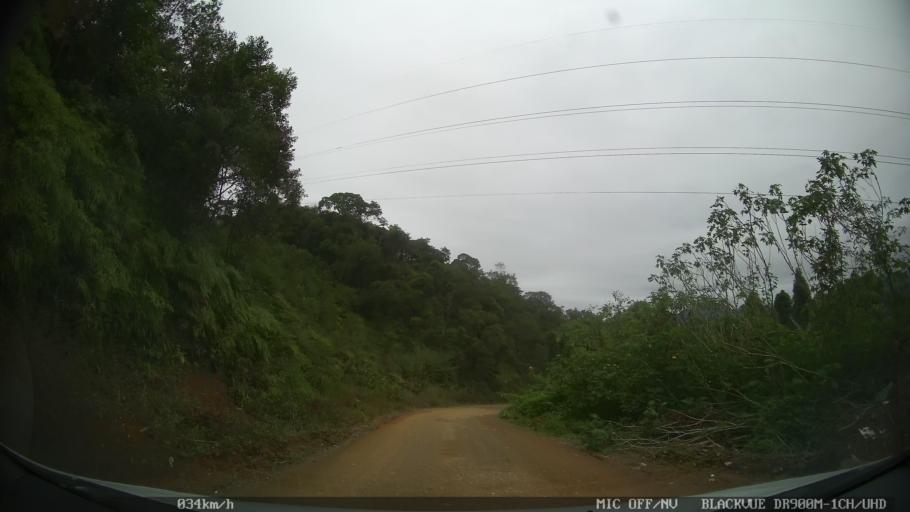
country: BR
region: Santa Catarina
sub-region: Joinville
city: Joinville
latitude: -26.2719
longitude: -48.9021
